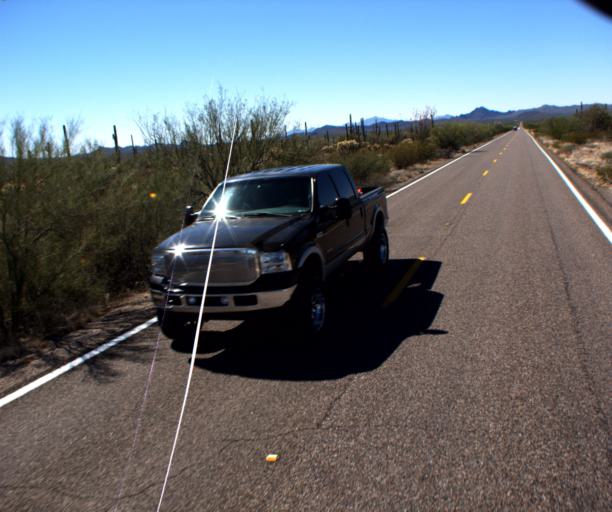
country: MX
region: Sonora
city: Sonoyta
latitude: 32.0630
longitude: -112.7862
